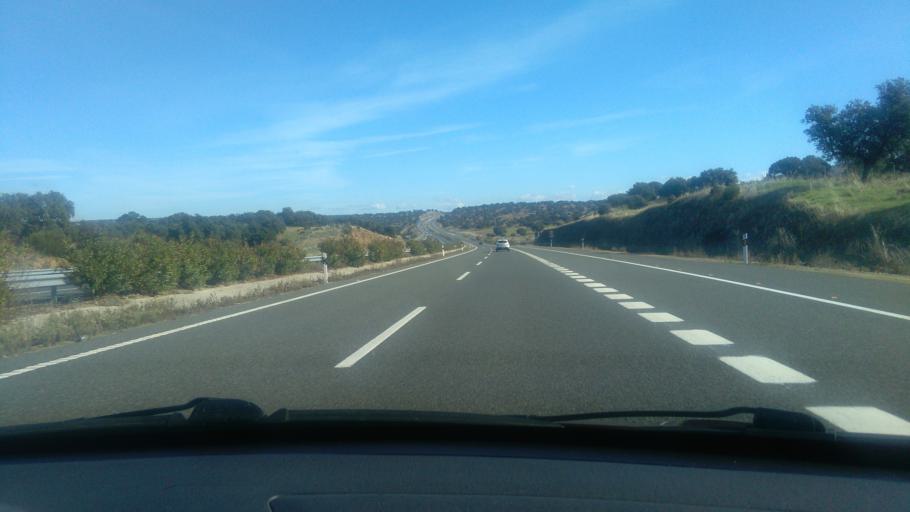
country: ES
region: Extremadura
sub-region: Provincia de Caceres
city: Plasenzuela
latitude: 39.4403
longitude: -6.0647
